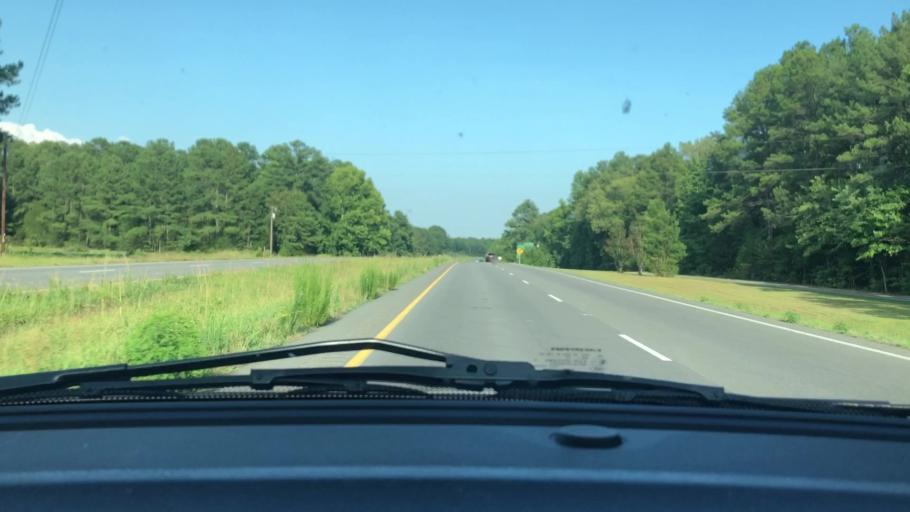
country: US
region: North Carolina
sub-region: Chatham County
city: Farmville
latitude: 35.5558
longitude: -79.2816
